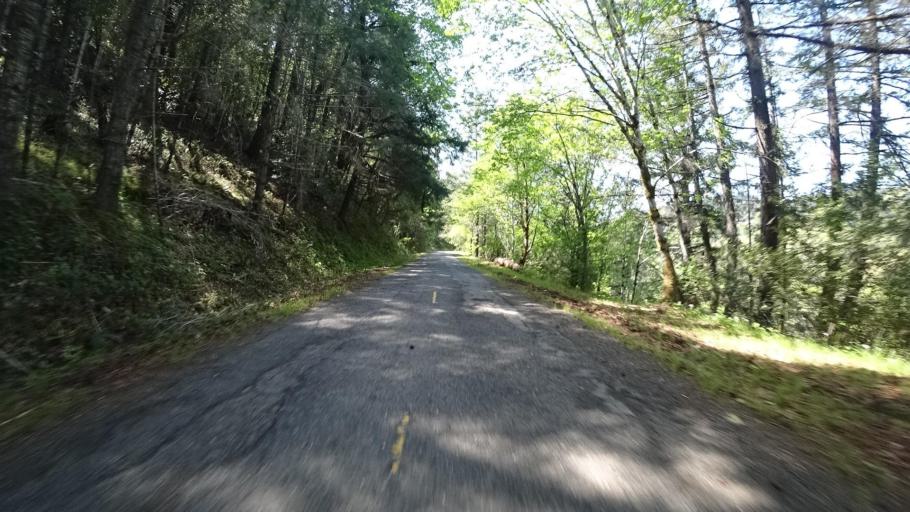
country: US
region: California
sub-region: Humboldt County
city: Redway
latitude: 40.2329
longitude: -123.6412
